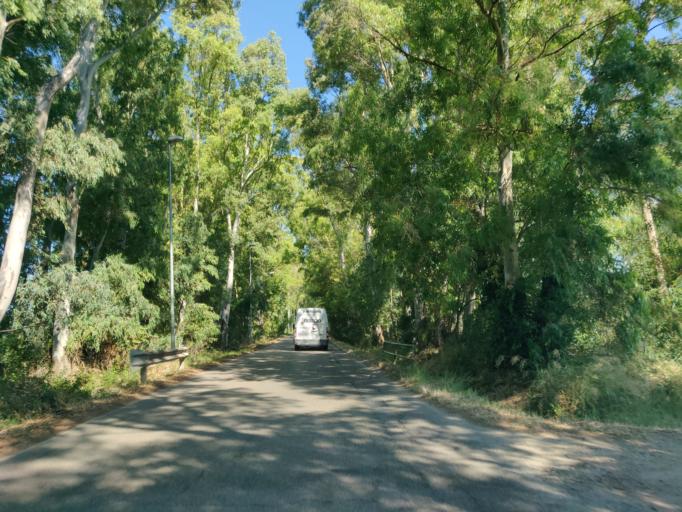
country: IT
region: Latium
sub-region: Citta metropolitana di Roma Capitale
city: Aurelia
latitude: 42.1595
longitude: 11.7494
